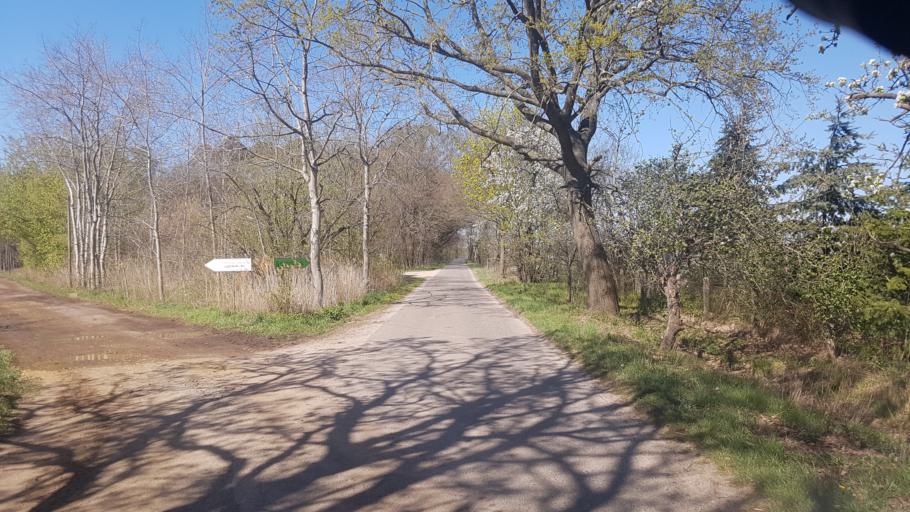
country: DE
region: Brandenburg
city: Sonnewalde
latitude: 51.7140
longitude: 13.6252
